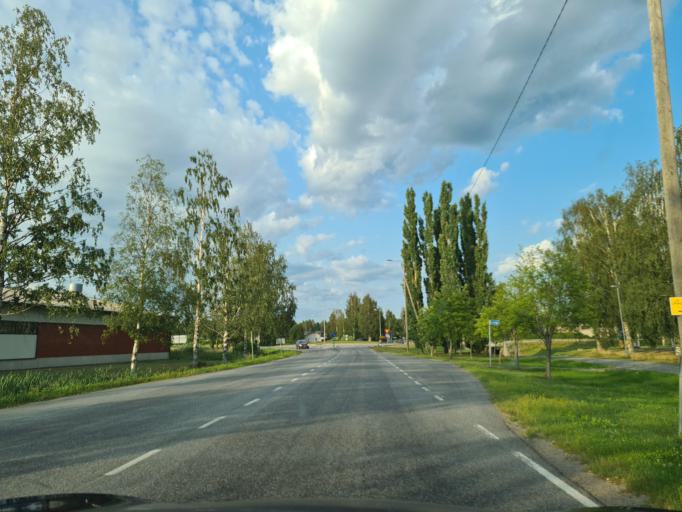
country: FI
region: Southern Ostrobothnia
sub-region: Seinaejoki
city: Lapua
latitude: 62.9756
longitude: 23.0211
